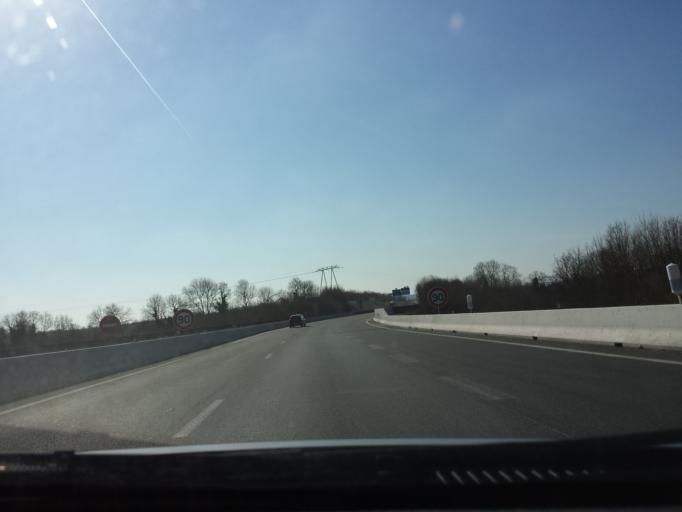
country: FR
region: Picardie
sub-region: Departement de la Somme
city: Saleux
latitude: 49.8526
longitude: 2.2467
